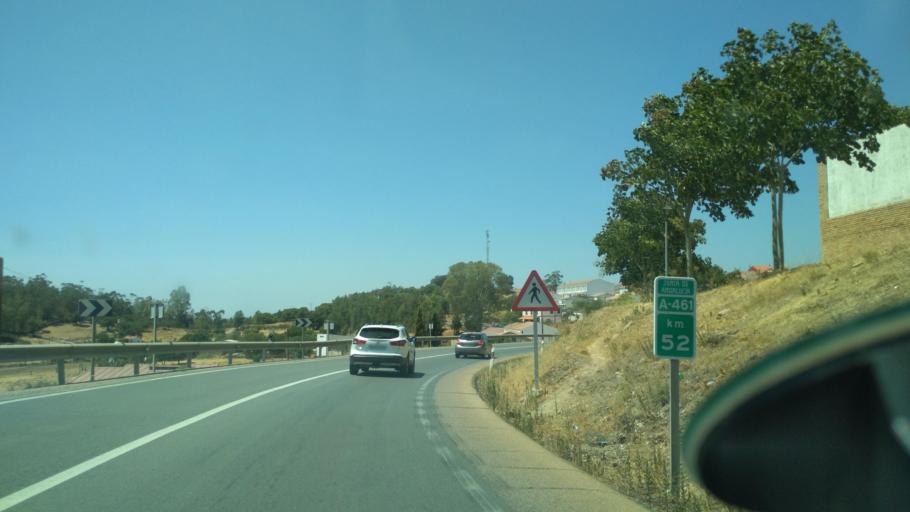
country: ES
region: Andalusia
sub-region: Provincia de Huelva
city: Zalamea la Real
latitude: 37.6911
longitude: -6.6288
